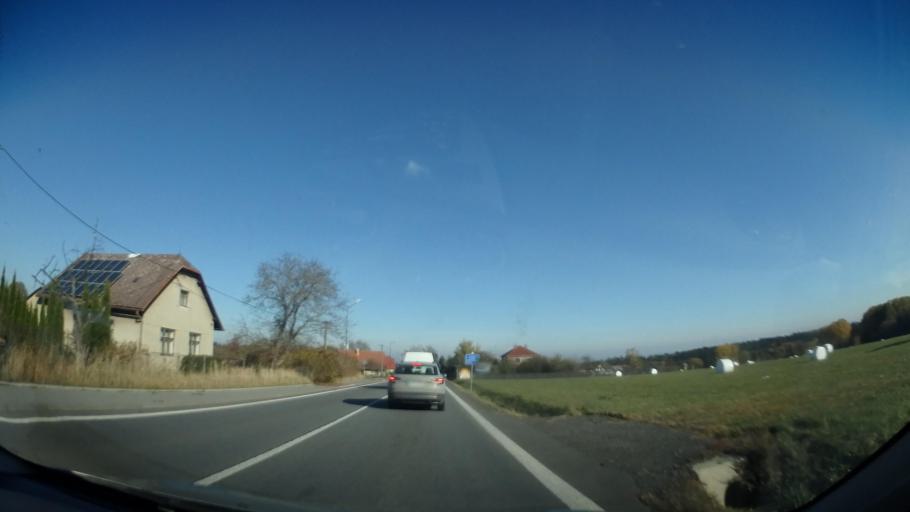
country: CZ
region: Pardubicky
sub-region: Okres Chrudim
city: Nasavrky
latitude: 49.8246
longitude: 15.8200
